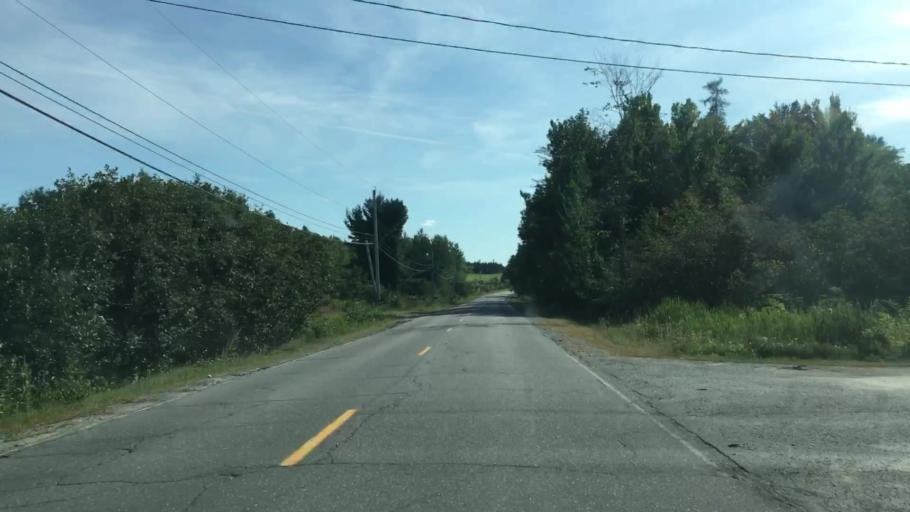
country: US
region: Maine
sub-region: Penobscot County
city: Lincoln
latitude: 45.3241
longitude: -68.5327
